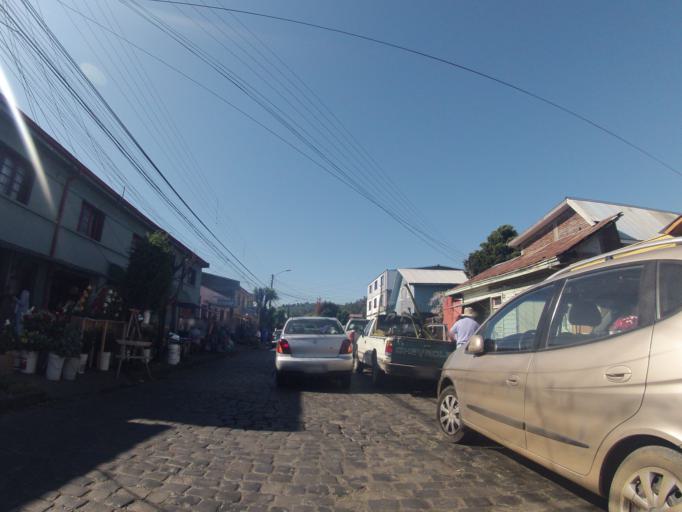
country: CL
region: Araucania
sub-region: Provincia de Cautin
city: Temuco
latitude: -38.7339
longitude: -72.5974
